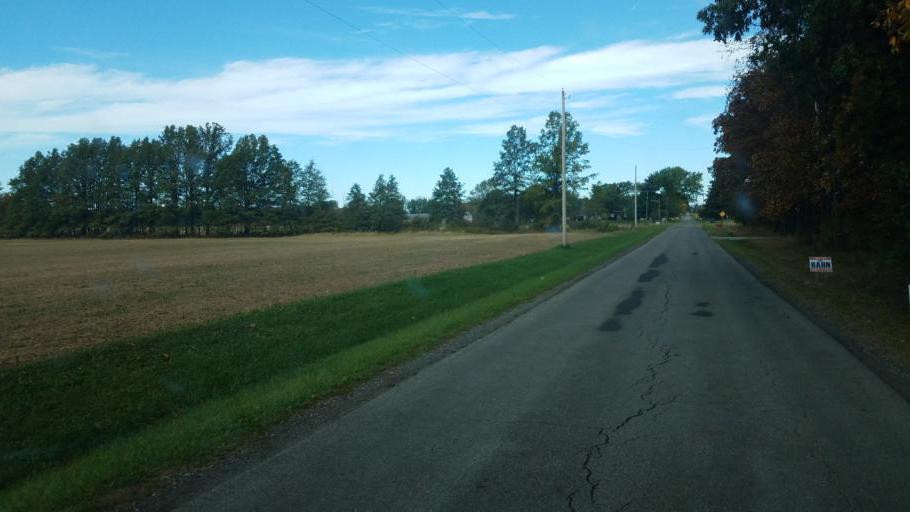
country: US
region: Ohio
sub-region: Huron County
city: Wakeman
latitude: 41.2518
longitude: -82.4668
